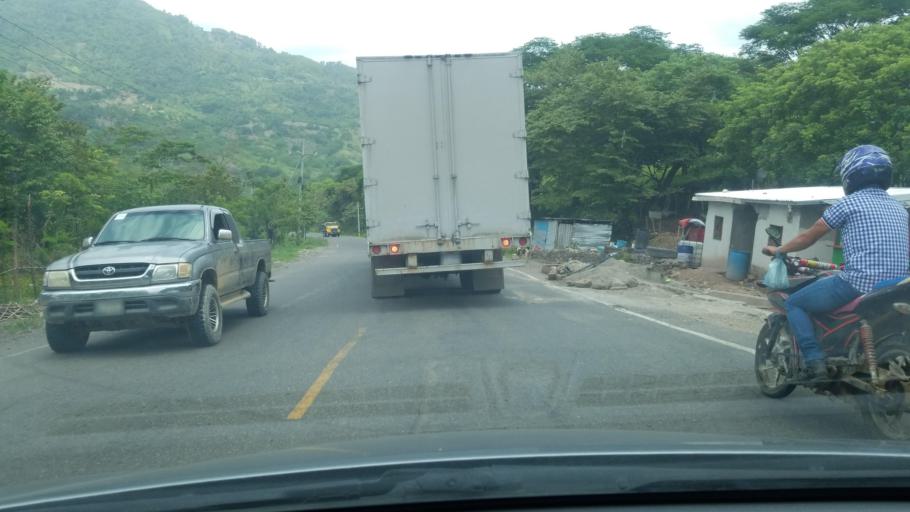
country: HN
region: Copan
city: Santa Rosa de Copan
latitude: 14.7207
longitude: -88.7718
